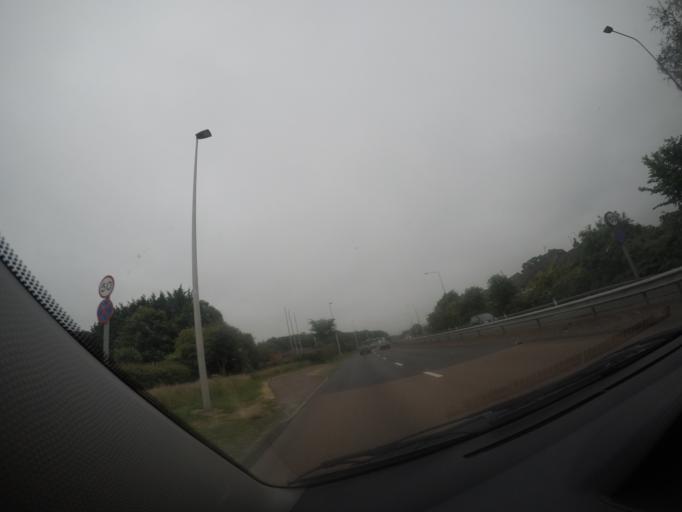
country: GB
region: Scotland
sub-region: Angus
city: Muirhead
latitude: 56.4770
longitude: -3.0383
